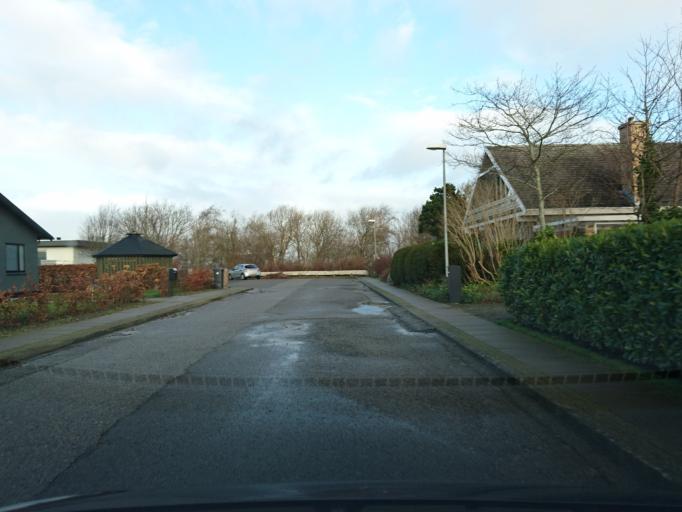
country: DK
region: North Denmark
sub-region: Alborg Kommune
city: Aalborg
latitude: 57.0164
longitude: 9.9413
